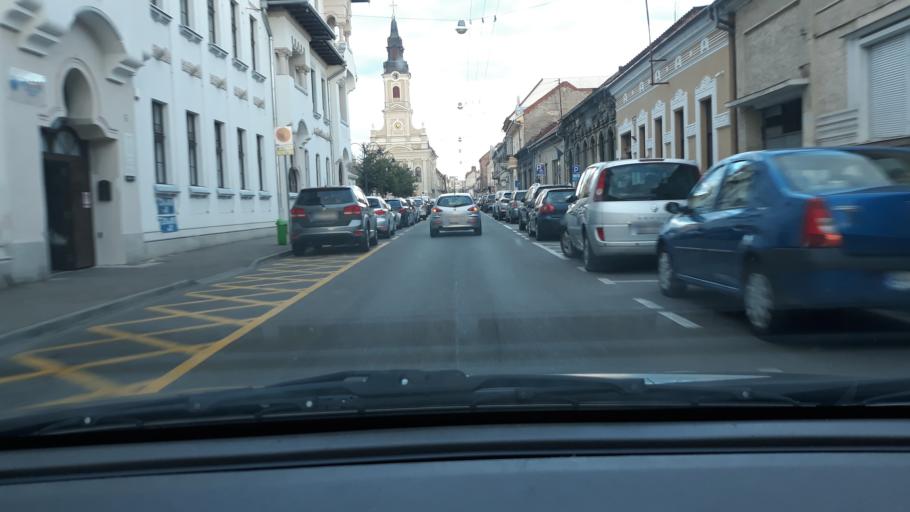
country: RO
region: Bihor
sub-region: Comuna Biharea
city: Oradea
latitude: 47.0542
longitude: 21.9262
